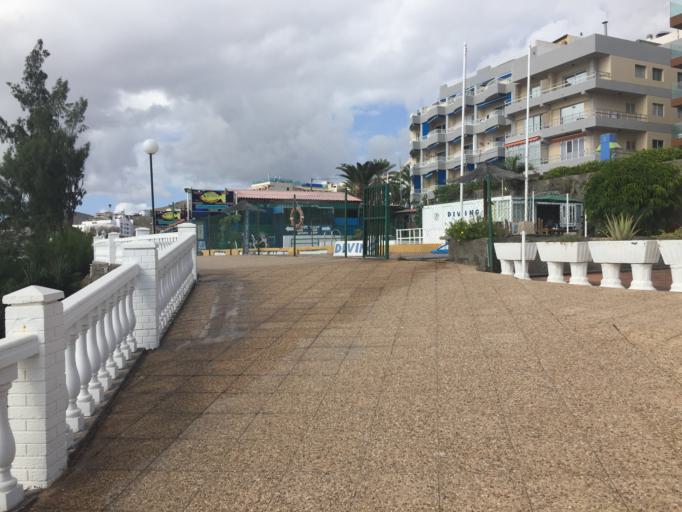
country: ES
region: Canary Islands
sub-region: Provincia de Las Palmas
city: Puerto Rico
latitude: 27.7604
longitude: -15.6841
